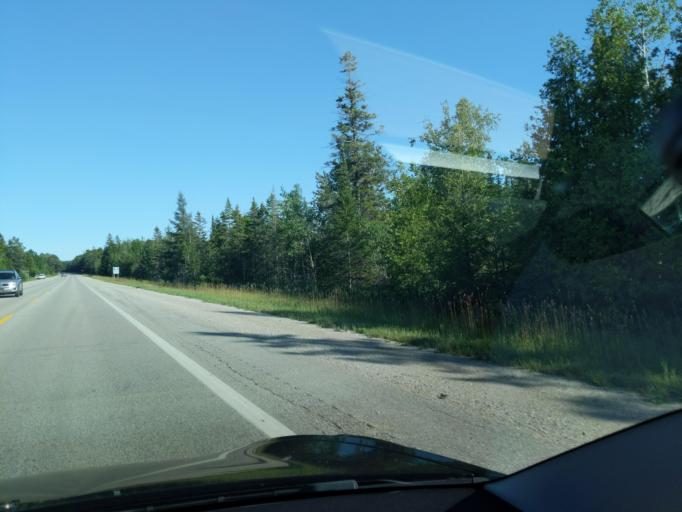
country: US
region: Michigan
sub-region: Mackinac County
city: Saint Ignace
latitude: 45.7539
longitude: -84.6942
